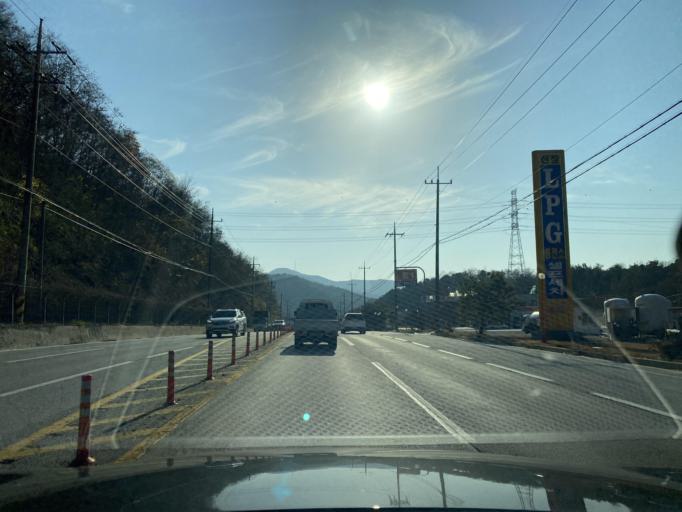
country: KR
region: Chungcheongnam-do
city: Asan
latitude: 36.7675
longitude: 126.9257
